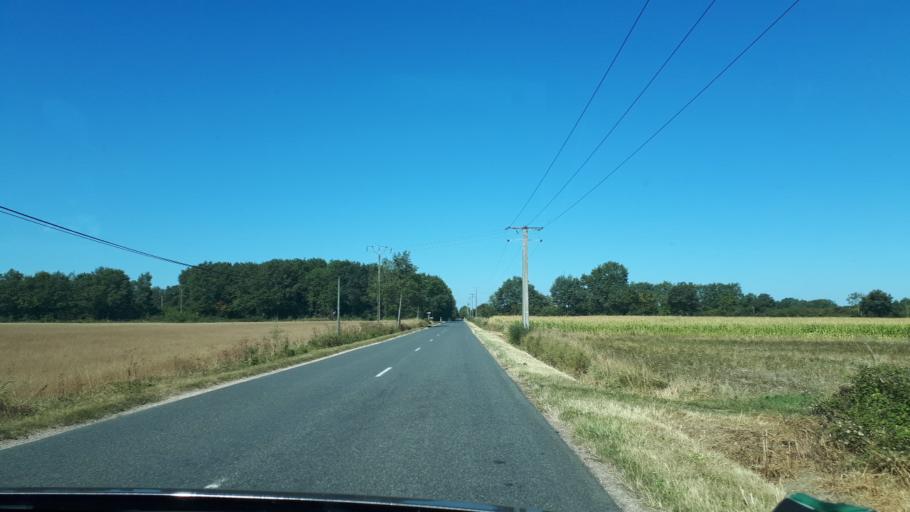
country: FR
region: Centre
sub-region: Departement du Loiret
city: Coullons
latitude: 47.6189
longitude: 2.5280
